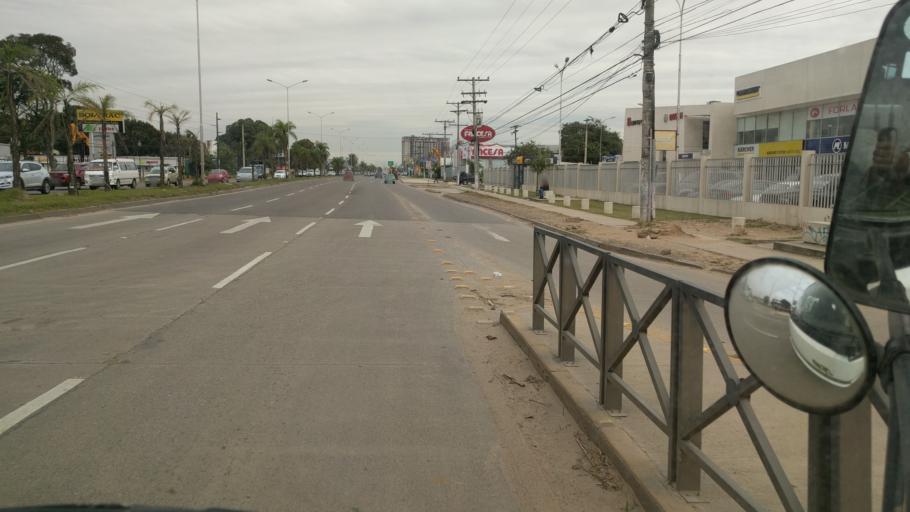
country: BO
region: Santa Cruz
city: Santa Cruz de la Sierra
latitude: -17.7164
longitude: -63.1622
